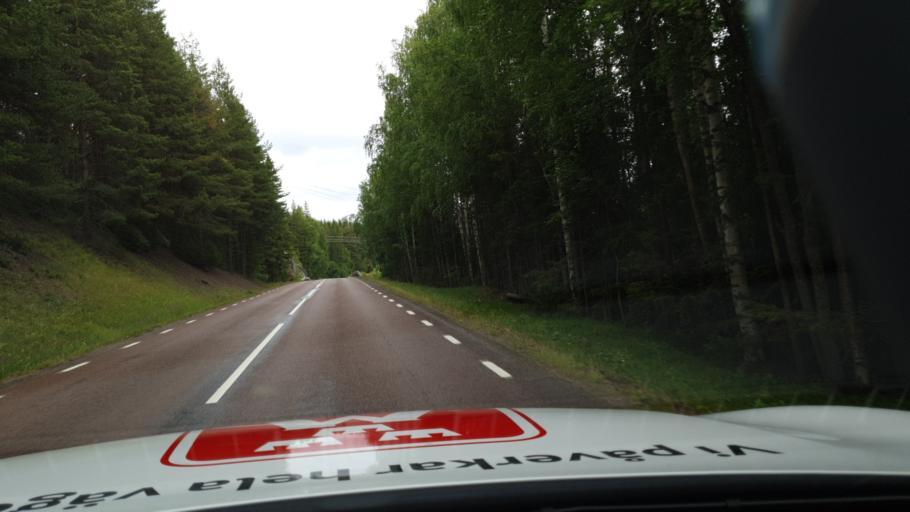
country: SE
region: Vaesternorrland
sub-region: Solleftea Kommun
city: As
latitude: 63.5871
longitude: 16.3240
